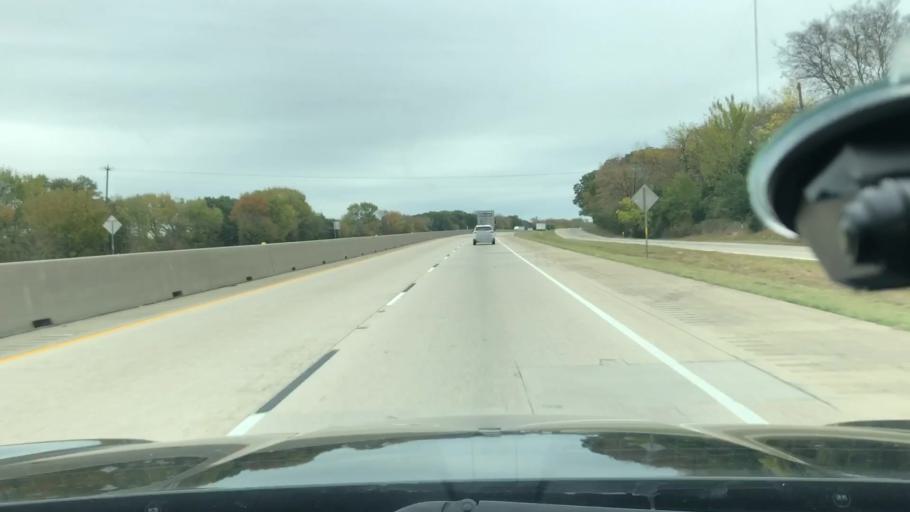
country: US
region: Texas
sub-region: Hopkins County
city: Sulphur Springs
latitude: 33.1269
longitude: -95.7465
